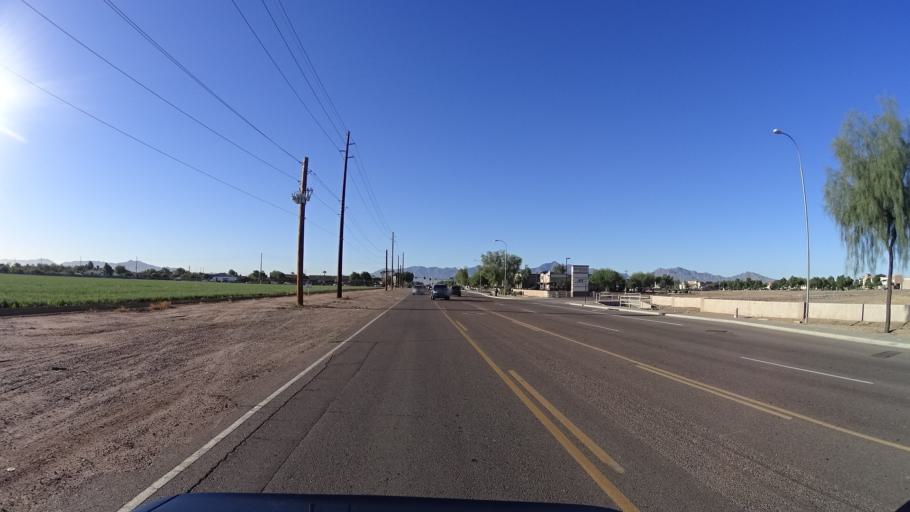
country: US
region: Arizona
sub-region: Maricopa County
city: Tolleson
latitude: 33.4251
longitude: -112.2212
